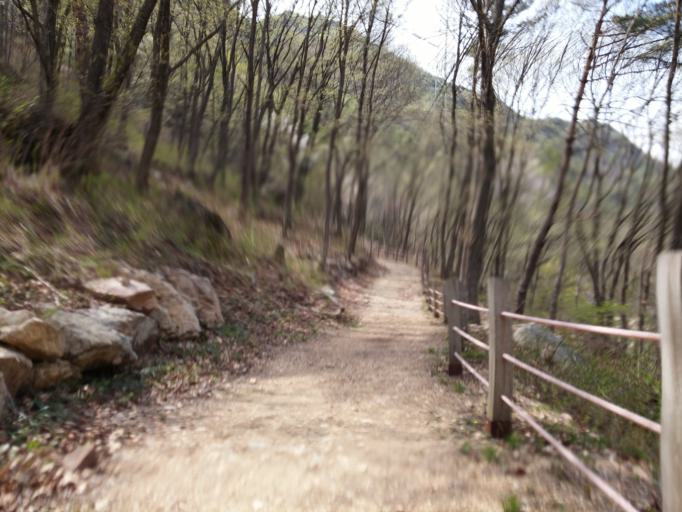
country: KR
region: Chungcheongbuk-do
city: Okcheon
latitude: 36.2364
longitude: 127.5589
